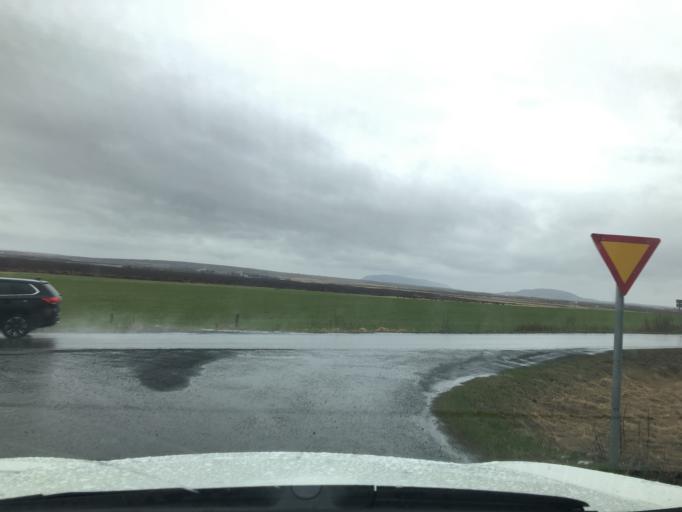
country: IS
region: South
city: Selfoss
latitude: 64.2392
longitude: -20.5506
